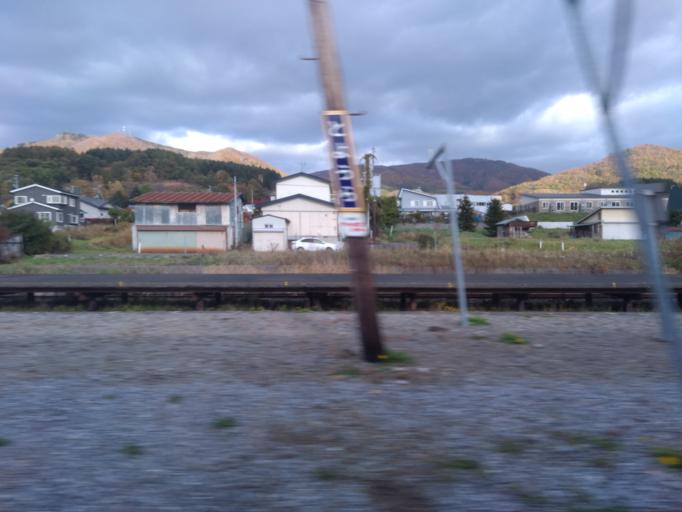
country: JP
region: Hokkaido
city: Date
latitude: 42.5803
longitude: 140.7151
